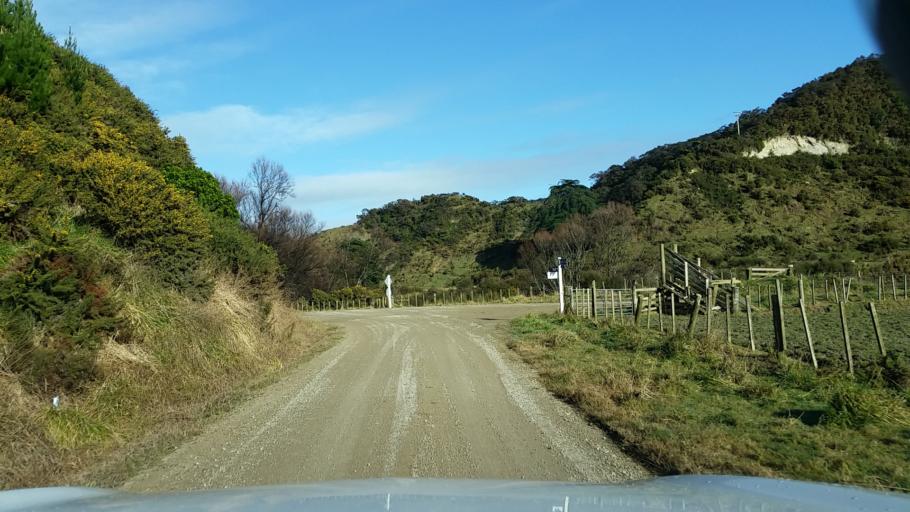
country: NZ
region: Taranaki
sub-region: South Taranaki District
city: Patea
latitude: -39.6968
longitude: 174.7411
